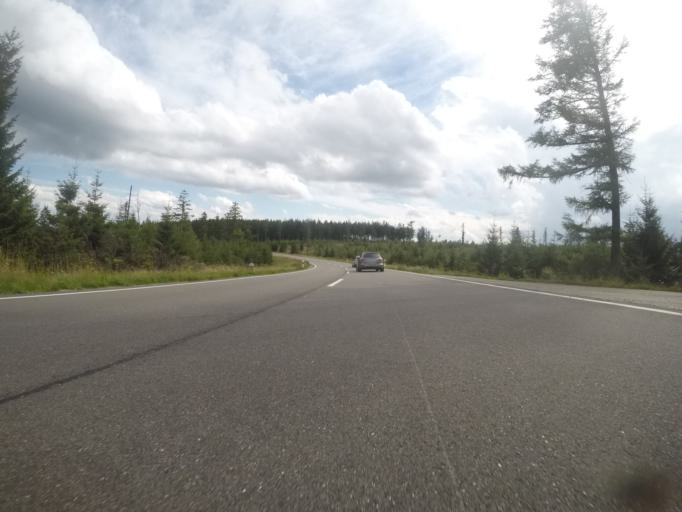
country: DE
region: Baden-Wuerttemberg
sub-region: Freiburg Region
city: Seebach
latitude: 48.5244
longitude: 8.2149
